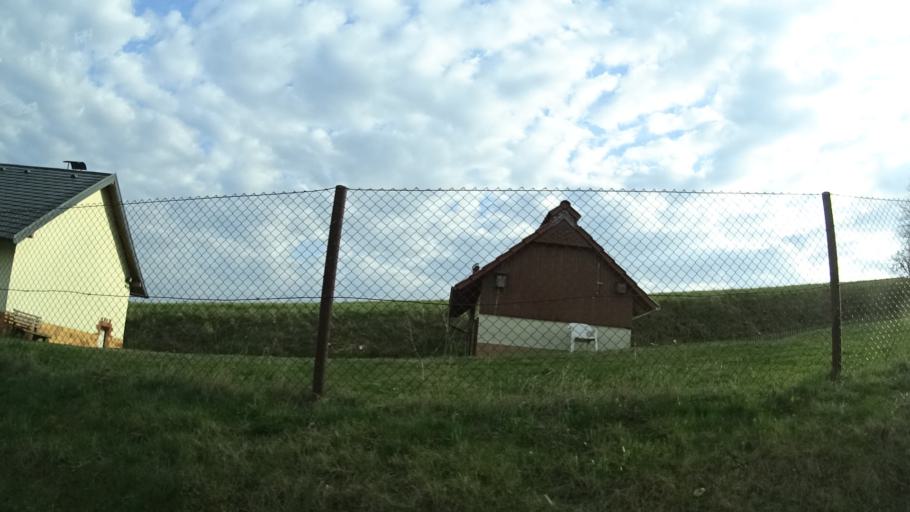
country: DE
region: Thuringia
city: Trusetal
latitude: 50.7816
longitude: 10.3938
